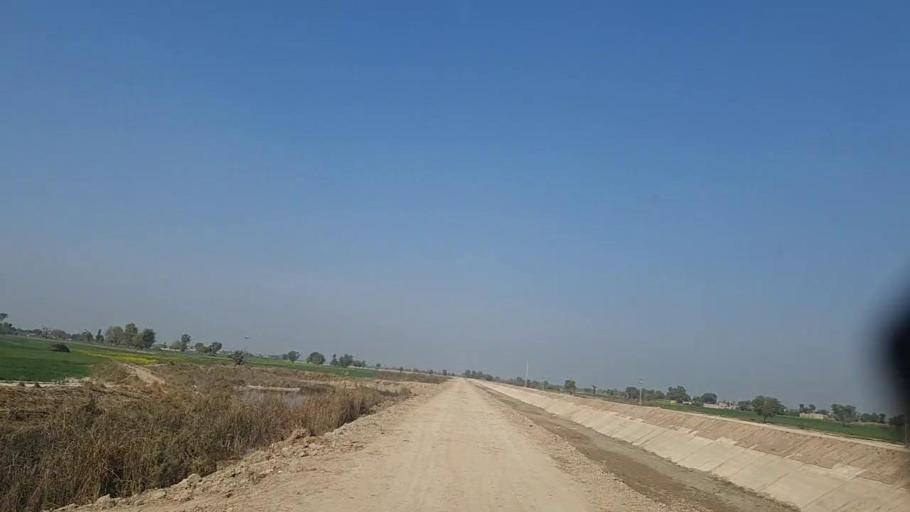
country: PK
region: Sindh
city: Sakrand
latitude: 26.1565
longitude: 68.3284
